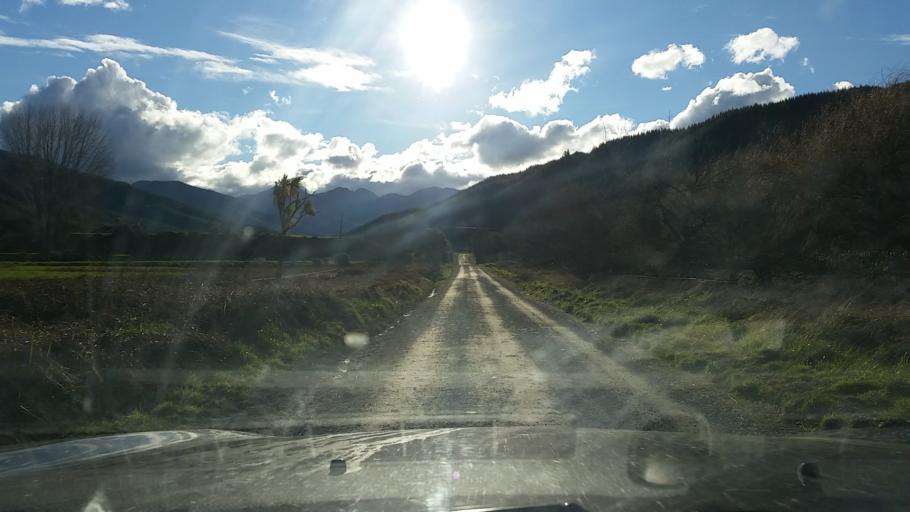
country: NZ
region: Nelson
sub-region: Nelson City
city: Nelson
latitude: -41.5672
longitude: 173.4508
